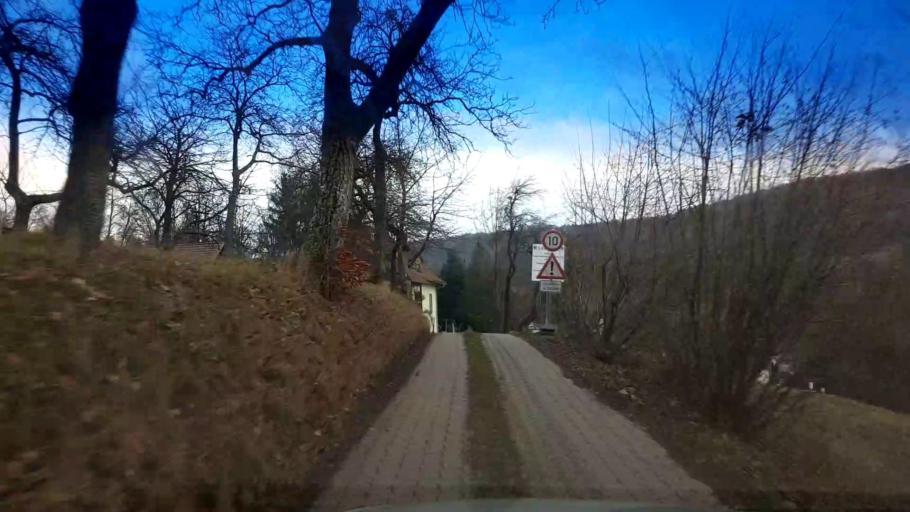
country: DE
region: Bavaria
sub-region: Upper Franconia
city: Schesslitz
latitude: 49.9980
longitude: 11.0786
